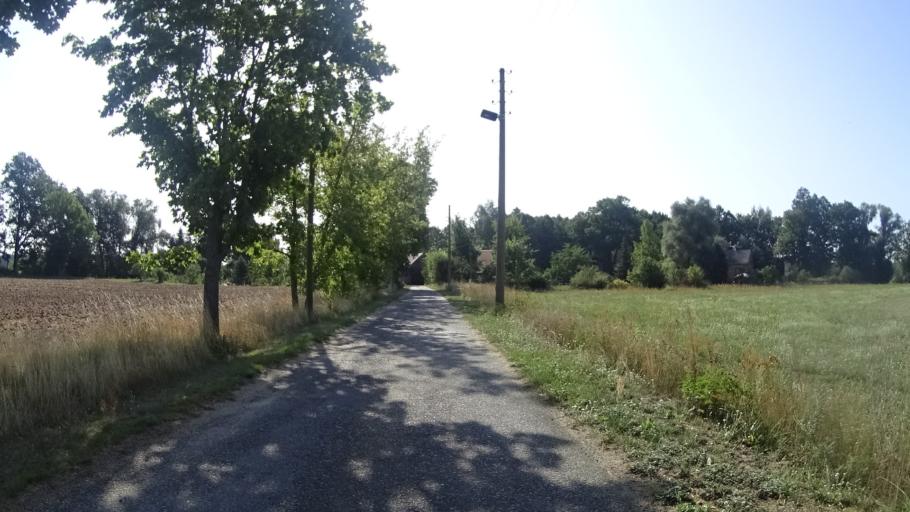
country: DE
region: Brandenburg
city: Neu Zauche
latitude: 51.9139
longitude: 14.0246
